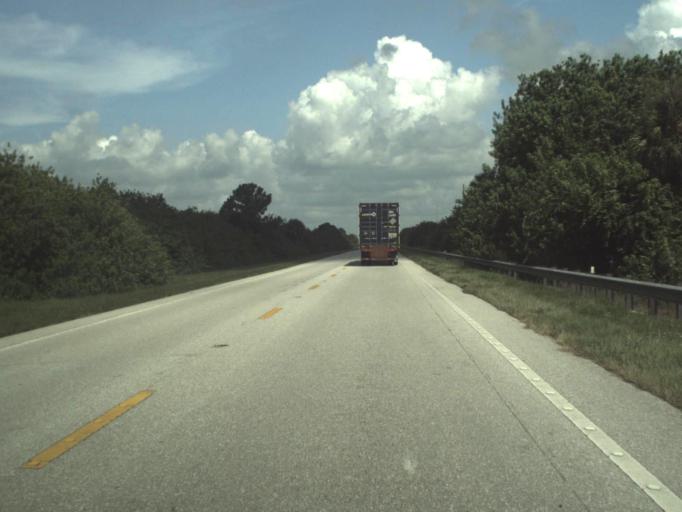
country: US
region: Florida
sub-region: Okeechobee County
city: Taylor Creek
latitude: 27.1522
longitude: -80.6669
